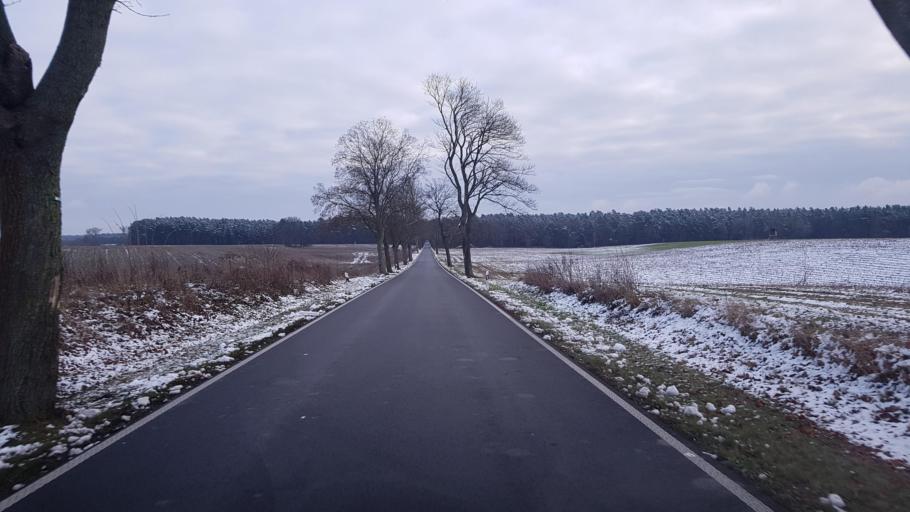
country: DE
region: Brandenburg
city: Strausberg
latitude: 52.5621
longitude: 13.9043
